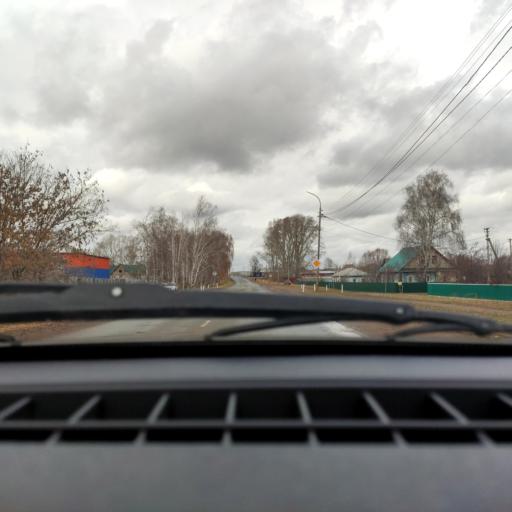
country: RU
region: Bashkortostan
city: Asanovo
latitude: 54.9579
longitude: 55.5525
